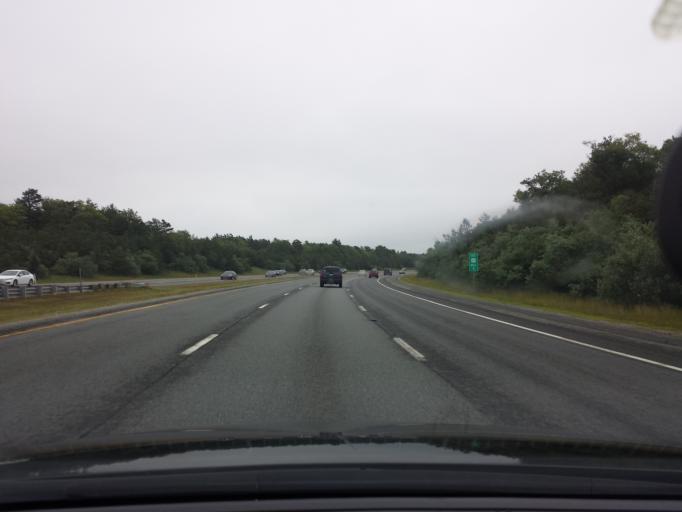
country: US
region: Massachusetts
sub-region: Barnstable County
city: Bourne
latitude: 41.7784
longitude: -70.5900
